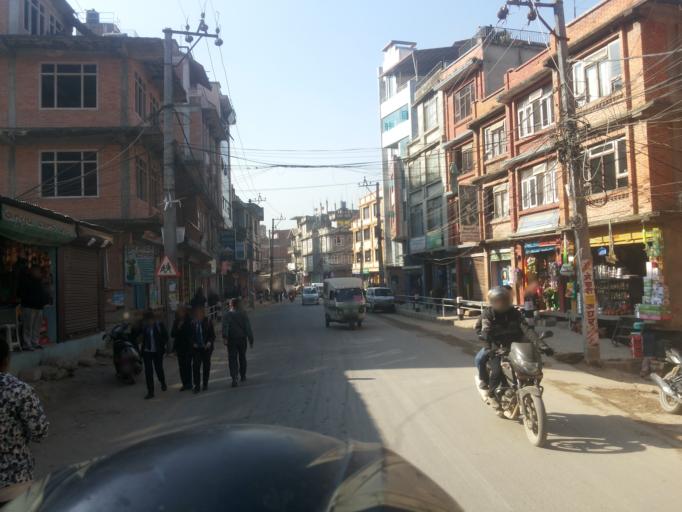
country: NP
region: Central Region
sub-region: Bagmati Zone
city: Patan
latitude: 27.6845
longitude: 85.3337
